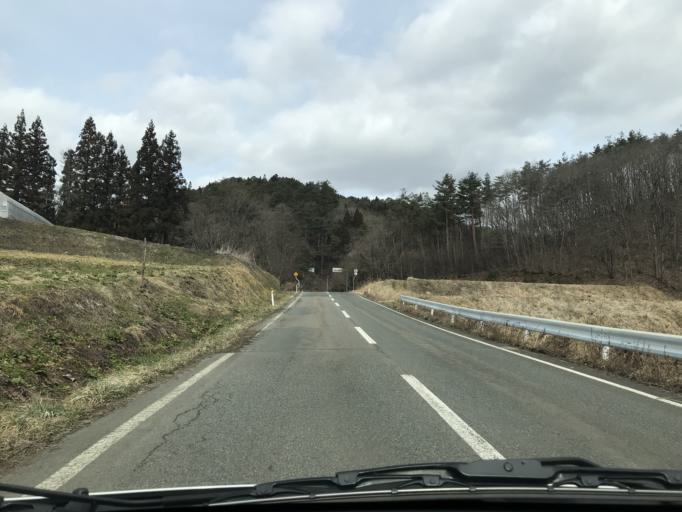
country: JP
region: Iwate
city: Kitakami
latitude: 39.2814
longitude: 141.3192
